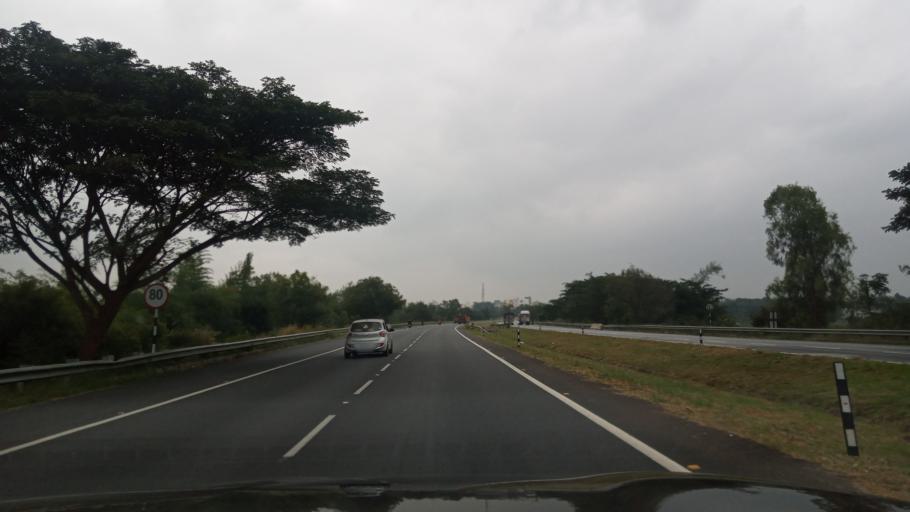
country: IN
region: Karnataka
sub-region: Bangalore Rural
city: Nelamangala
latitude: 13.0218
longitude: 77.4757
